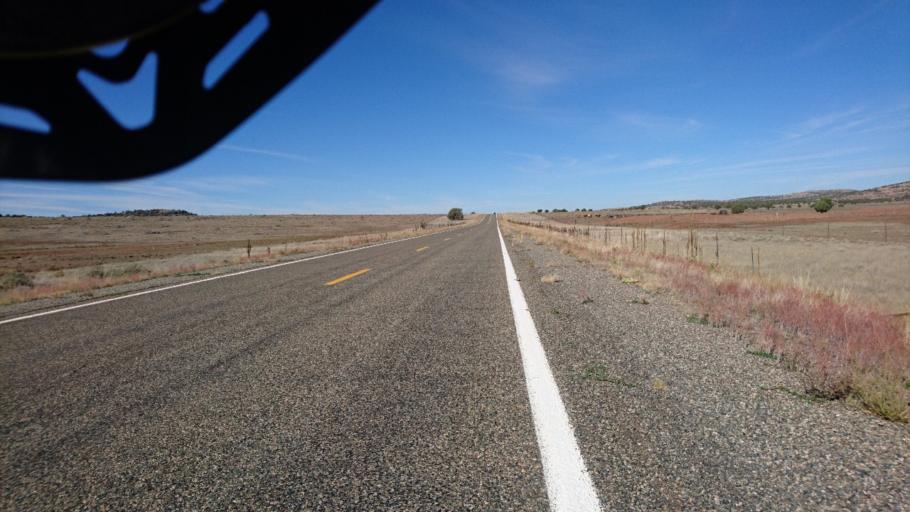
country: US
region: Arizona
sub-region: Yavapai County
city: Paulden
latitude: 35.2853
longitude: -112.7215
